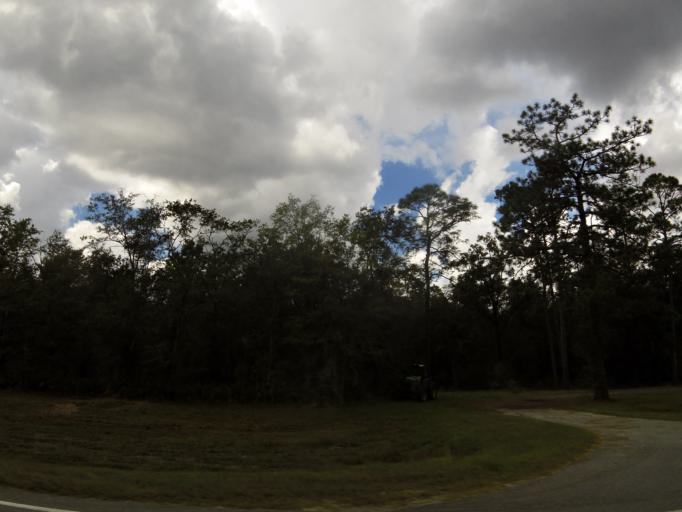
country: US
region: Georgia
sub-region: Brantley County
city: Nahunta
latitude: 31.1747
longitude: -81.9889
